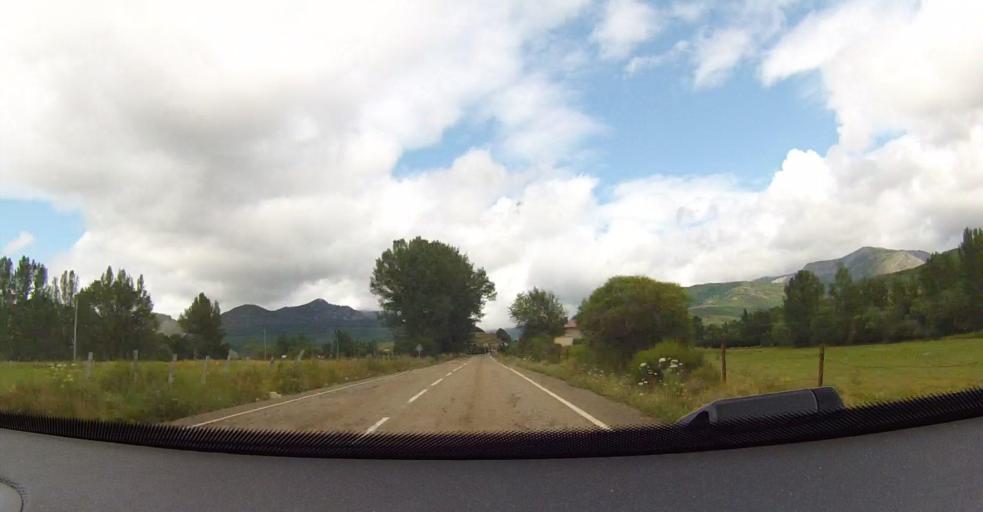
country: ES
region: Castille and Leon
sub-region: Provincia de Leon
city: Puebla de Lillo
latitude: 43.0000
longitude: -5.2661
